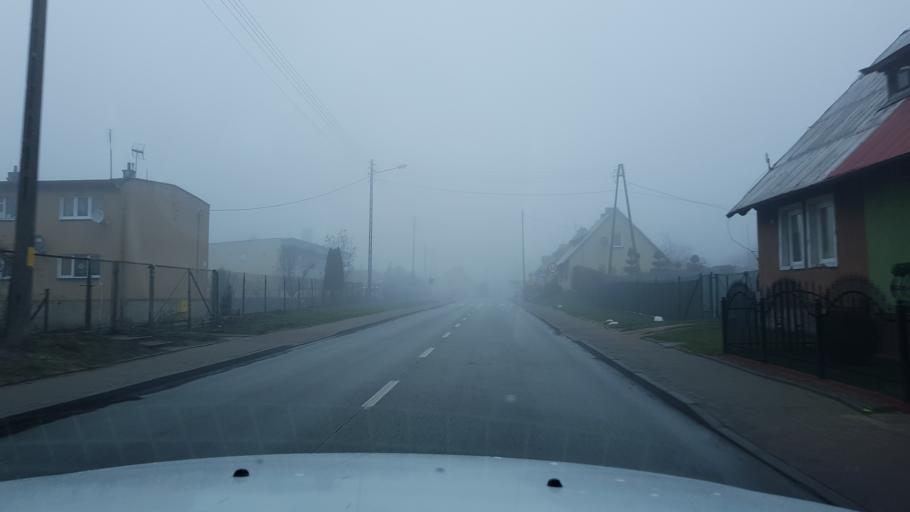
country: PL
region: West Pomeranian Voivodeship
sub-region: Powiat mysliborski
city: Mysliborz
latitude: 52.9494
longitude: 14.7907
